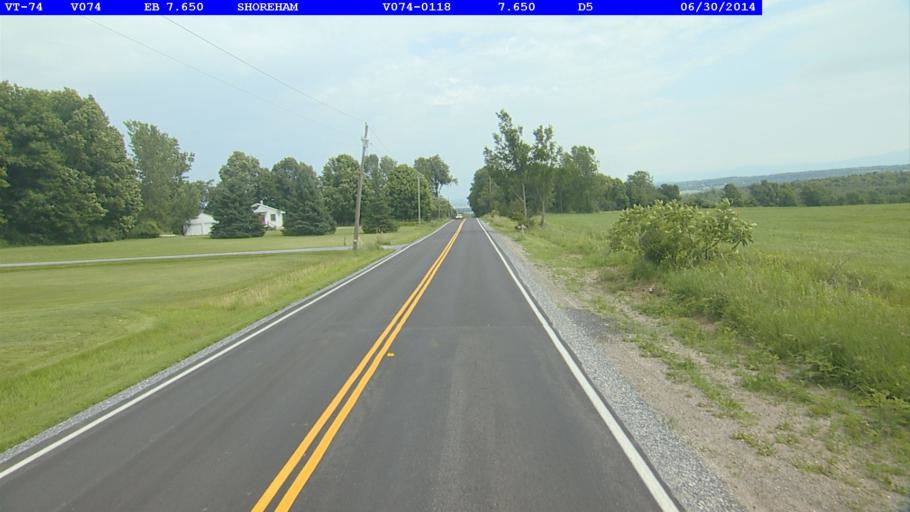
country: US
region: Vermont
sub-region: Addison County
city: Middlebury (village)
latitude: 43.9289
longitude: -73.2899
